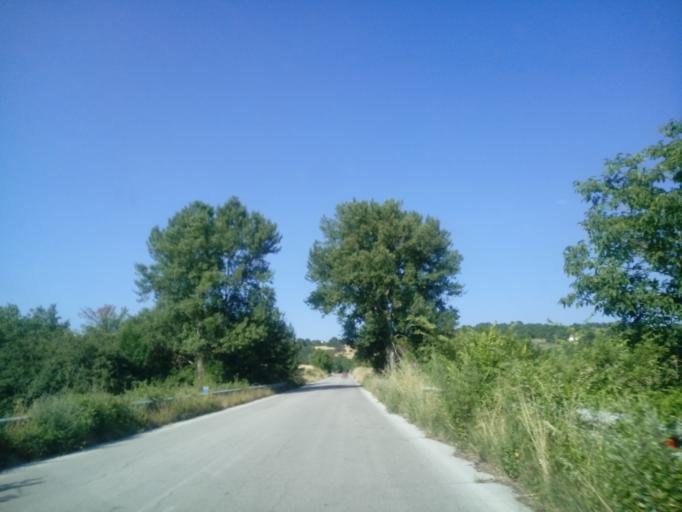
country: IT
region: Molise
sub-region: Provincia di Campobasso
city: Gildone
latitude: 41.5122
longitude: 14.7689
